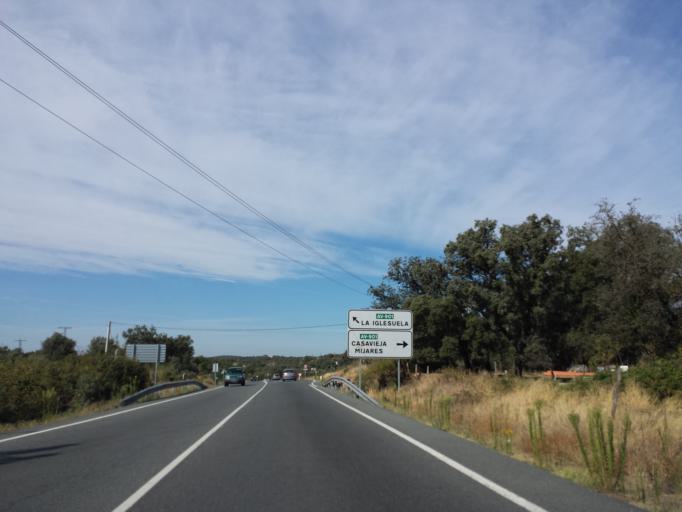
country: ES
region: Castille and Leon
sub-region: Provincia de Avila
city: Casavieja
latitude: 40.2706
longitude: -4.7503
